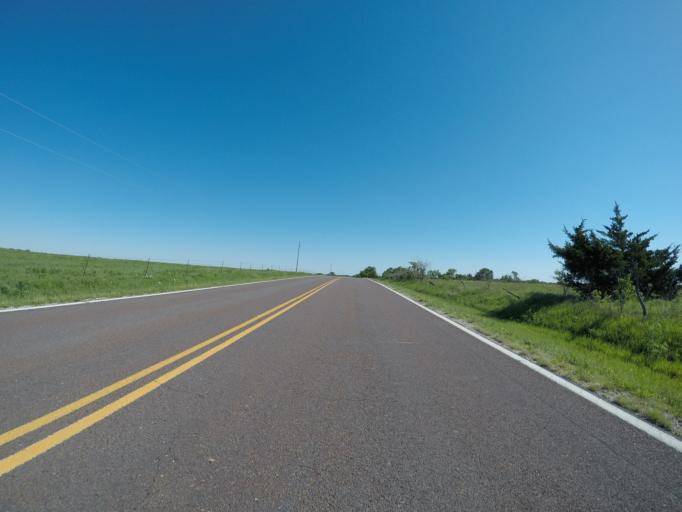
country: US
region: Kansas
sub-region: Osage County
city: Osage City
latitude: 38.7029
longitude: -96.0940
